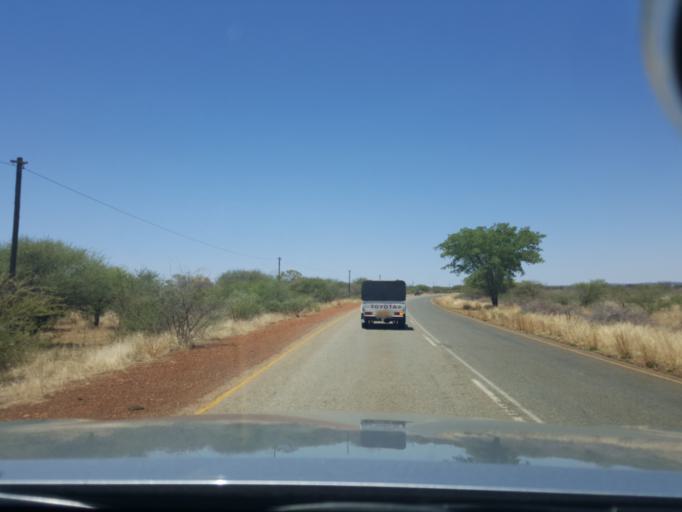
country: BW
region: South East
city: Otse
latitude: -25.1017
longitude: 25.9616
